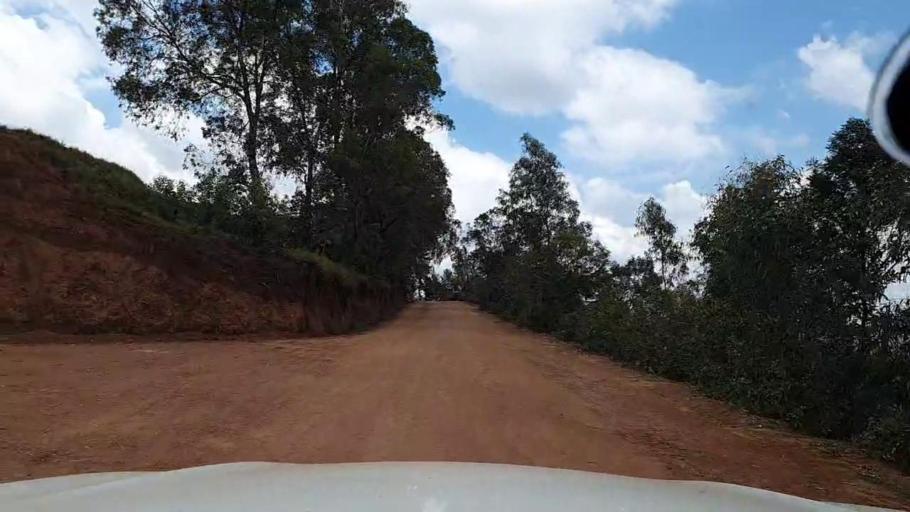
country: RW
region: Southern Province
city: Nzega
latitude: -2.7089
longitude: 29.5228
